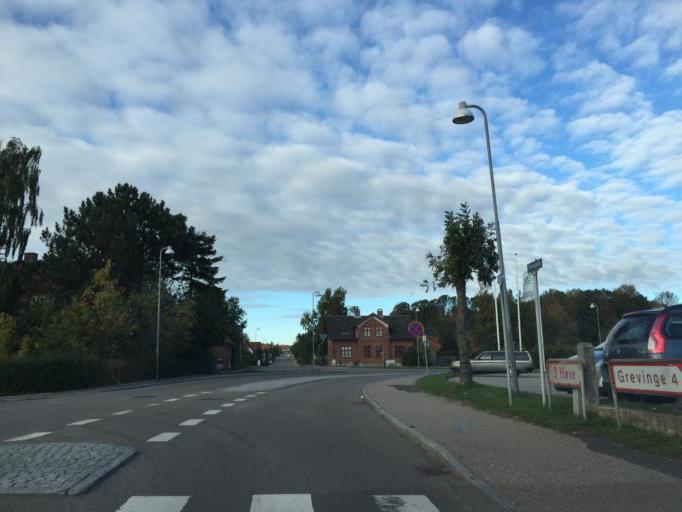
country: DK
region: Zealand
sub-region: Odsherred Kommune
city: Asnaes
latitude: 55.8123
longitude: 11.4982
